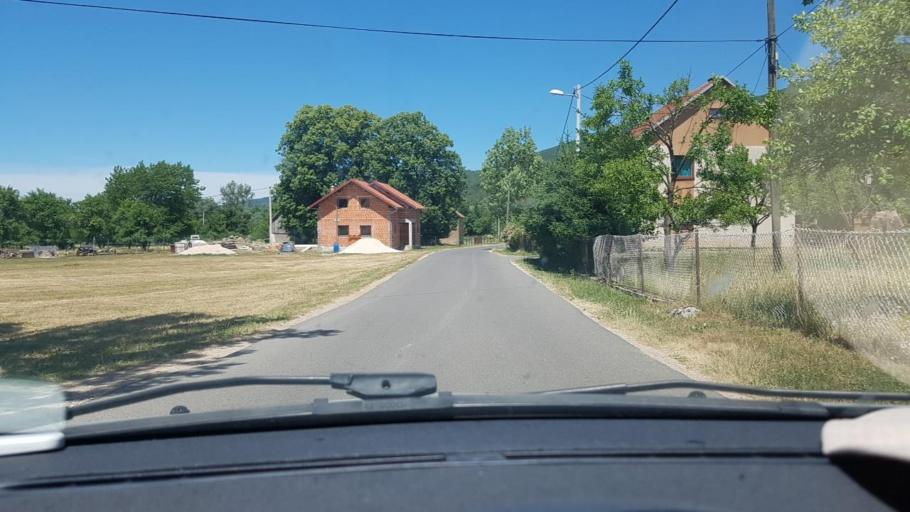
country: HR
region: Licko-Senjska
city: Otocac
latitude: 44.8108
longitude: 15.3590
